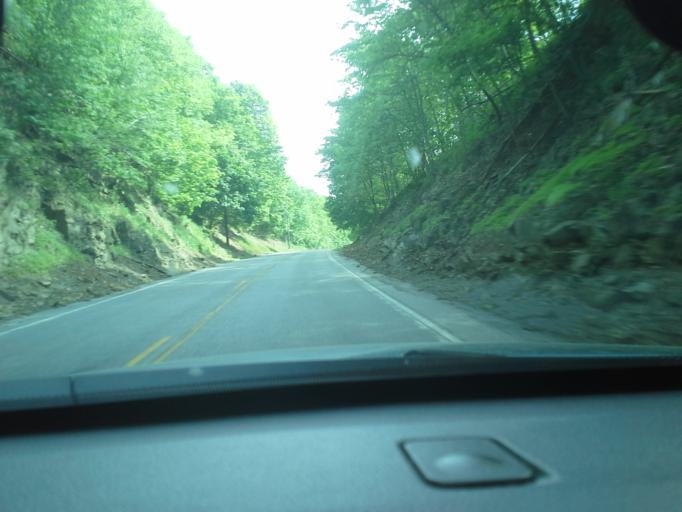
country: US
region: Pennsylvania
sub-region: Fulton County
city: McConnellsburg
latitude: 39.9057
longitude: -77.9664
